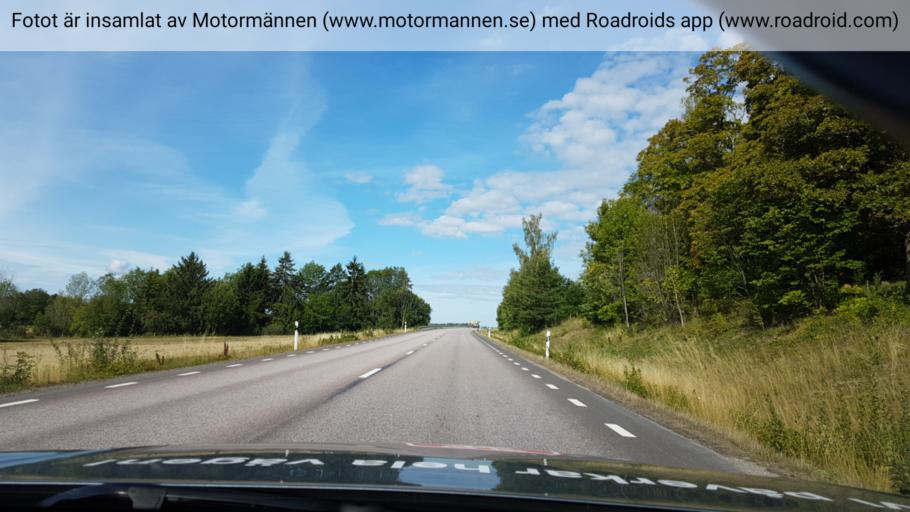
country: SE
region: Uppsala
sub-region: Osthammars Kommun
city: Bjorklinge
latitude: 59.9453
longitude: 17.4256
